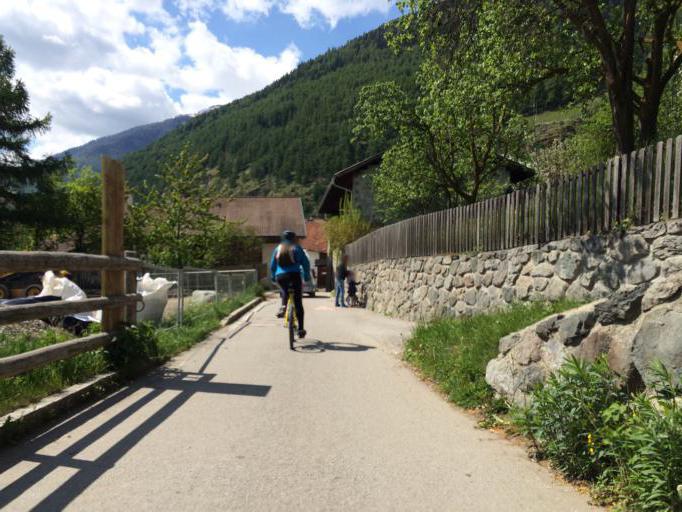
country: IT
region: Trentino-Alto Adige
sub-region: Bolzano
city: Malles Venosta
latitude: 46.6952
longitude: 10.5220
